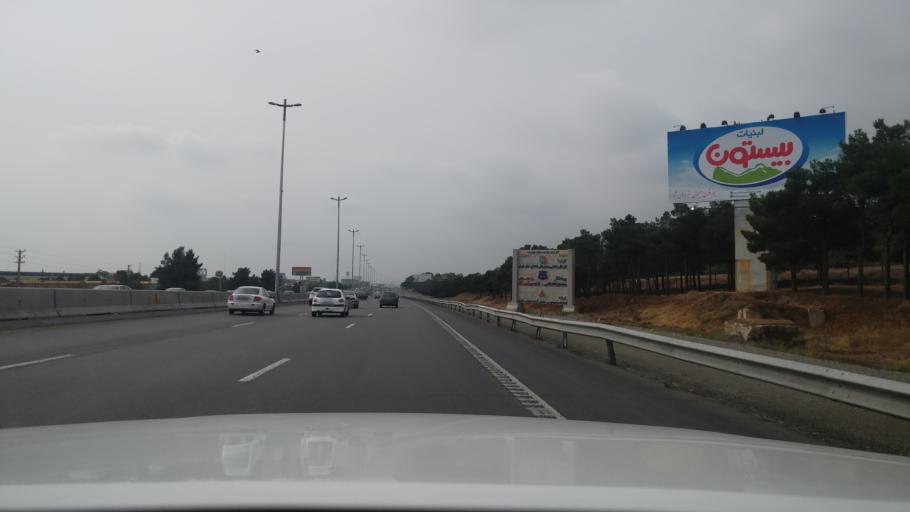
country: IR
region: Tehran
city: Shahr-e Qods
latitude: 35.7178
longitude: 51.2316
